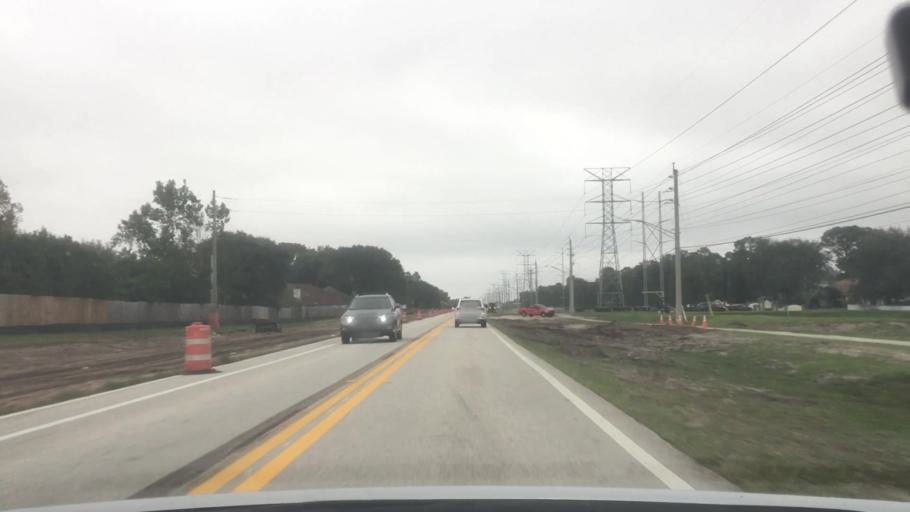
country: US
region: Florida
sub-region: Duval County
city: Atlantic Beach
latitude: 30.3494
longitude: -81.4897
